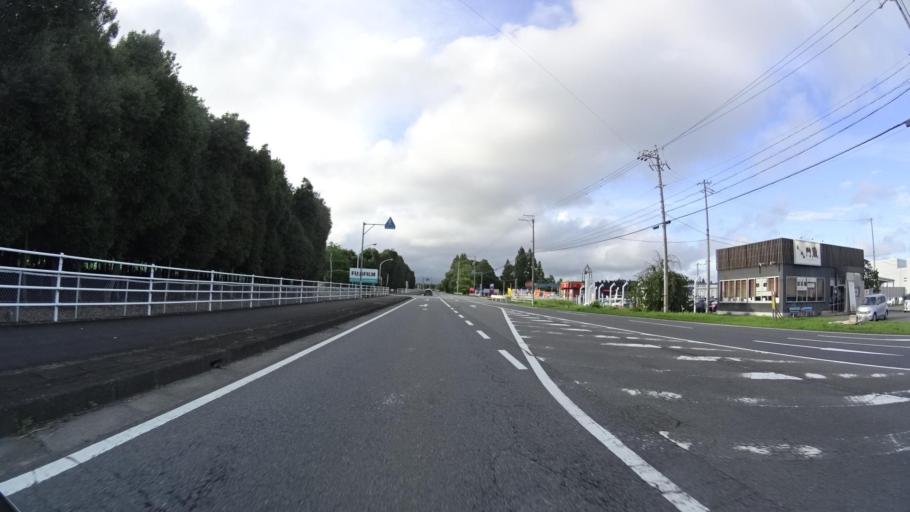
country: JP
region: Mie
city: Komono
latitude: 34.9227
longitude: 136.4924
